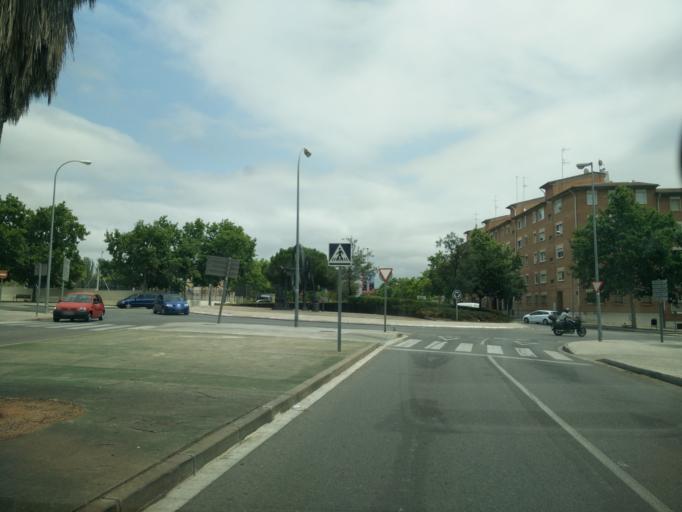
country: ES
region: Catalonia
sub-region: Provincia de Barcelona
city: Terrassa
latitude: 41.5801
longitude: 2.0174
